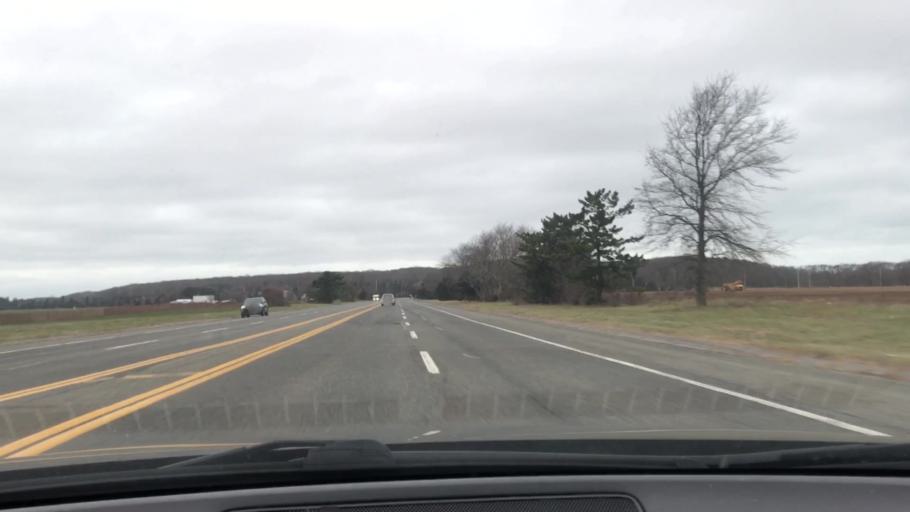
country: US
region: New York
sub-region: Suffolk County
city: Aquebogue
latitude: 40.9625
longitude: -72.6526
